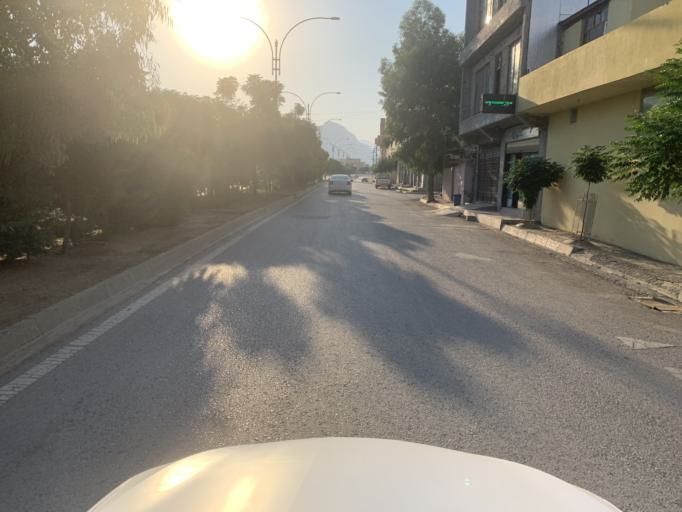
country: IQ
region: As Sulaymaniyah
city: Raniye
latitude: 36.2392
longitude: 44.8784
